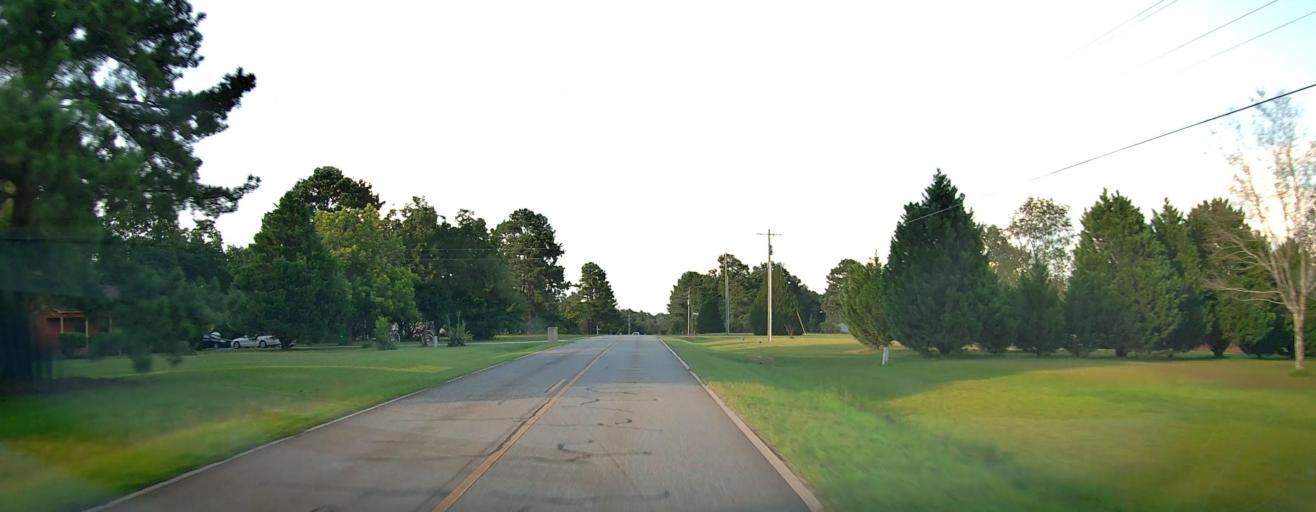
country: US
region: Georgia
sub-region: Peach County
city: Byron
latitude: 32.6189
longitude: -83.8286
